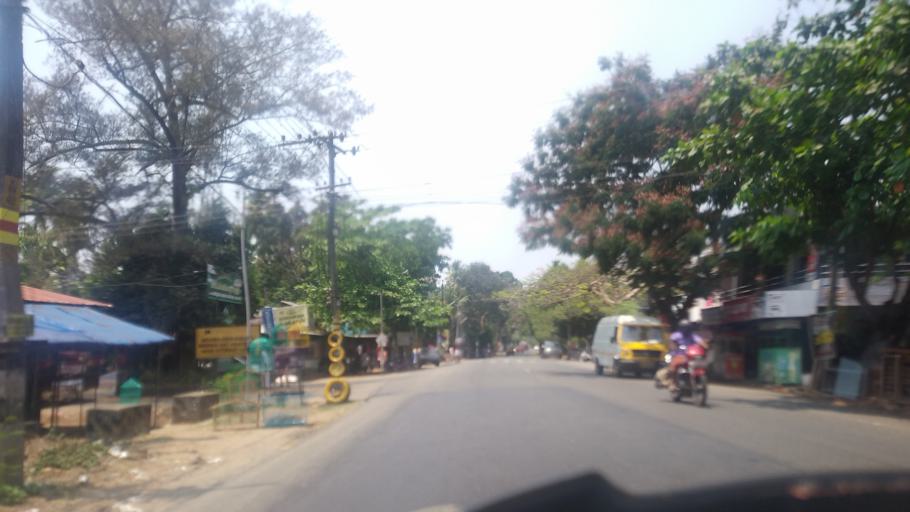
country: IN
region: Kerala
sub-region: Thrissur District
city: Kodungallur
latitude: 10.2633
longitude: 76.1811
